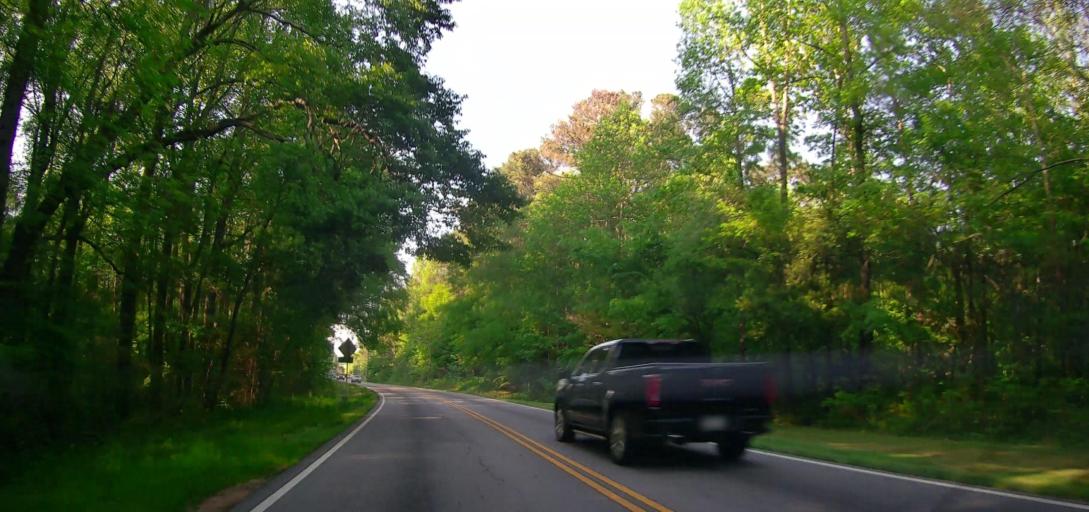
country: US
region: Georgia
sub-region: Newton County
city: Covington
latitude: 33.5963
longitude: -83.8762
